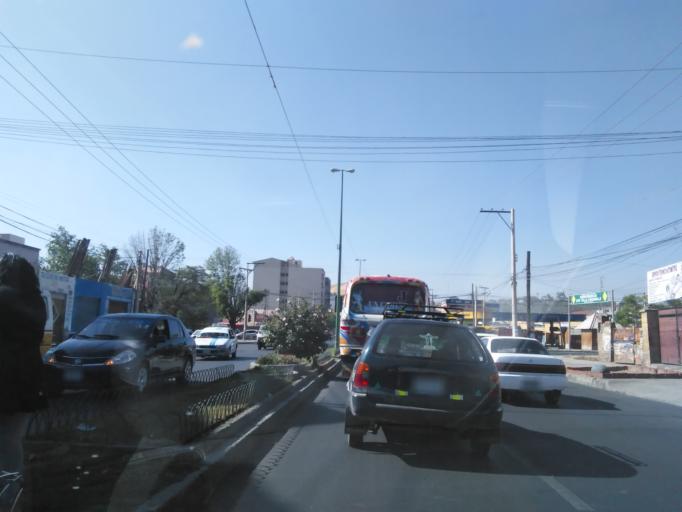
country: BO
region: Cochabamba
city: Cochabamba
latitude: -17.3979
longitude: -66.1660
